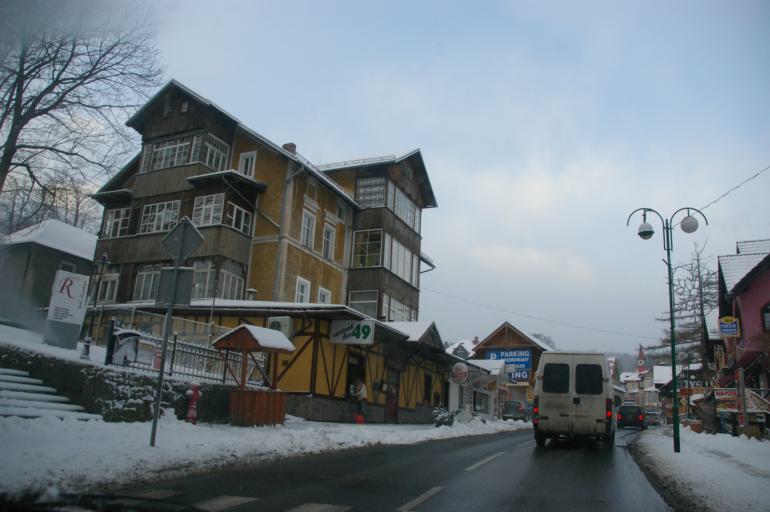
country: PL
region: Lower Silesian Voivodeship
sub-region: Powiat jeleniogorski
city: Karpacz
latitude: 50.7751
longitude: 15.7572
